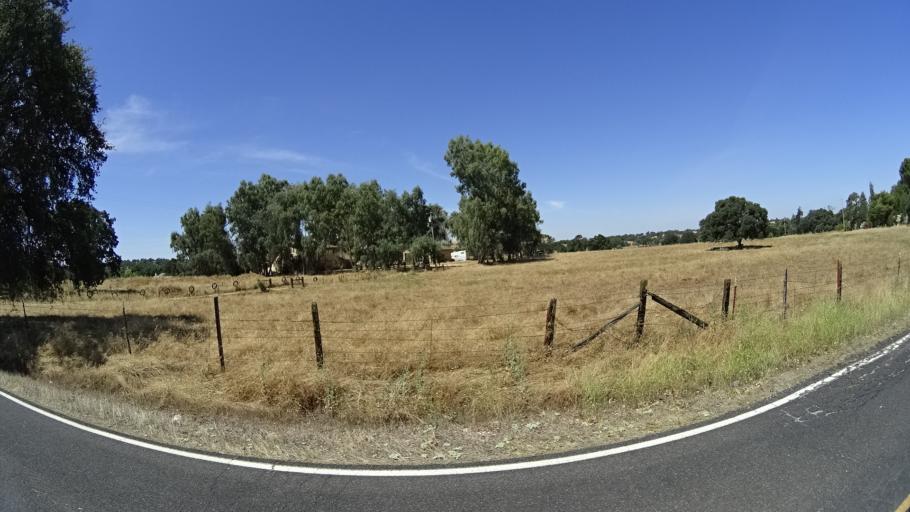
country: US
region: California
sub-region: Calaveras County
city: Rancho Calaveras
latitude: 38.1769
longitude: -120.9584
